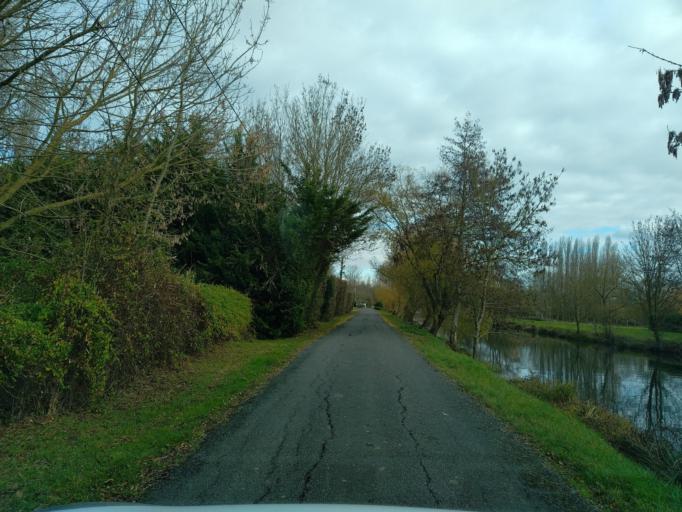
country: FR
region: Pays de la Loire
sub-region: Departement de la Vendee
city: Maillezais
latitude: 46.3220
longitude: -0.7672
